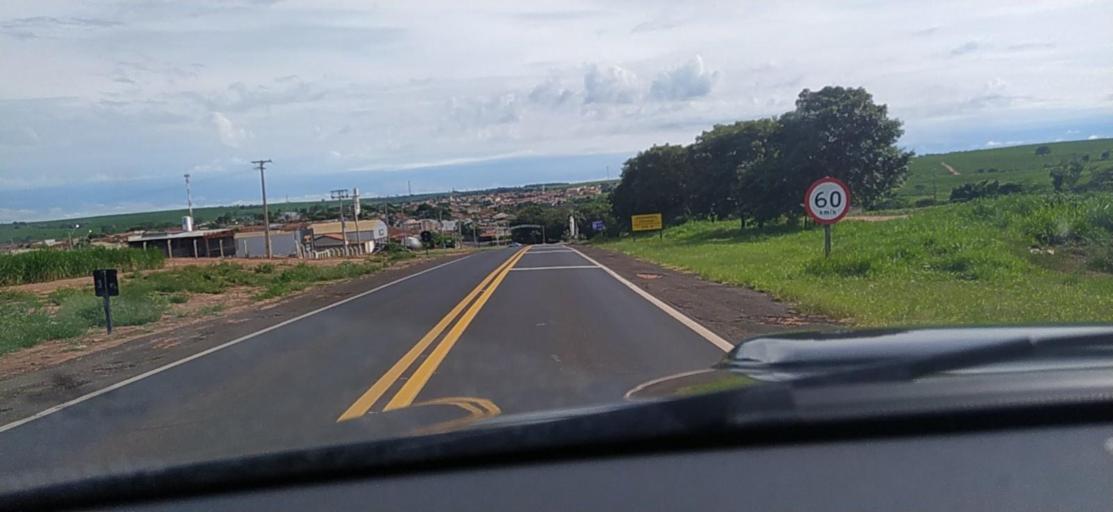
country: BR
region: Sao Paulo
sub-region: Catanduva
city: Catanduva
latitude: -21.0667
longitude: -49.0640
